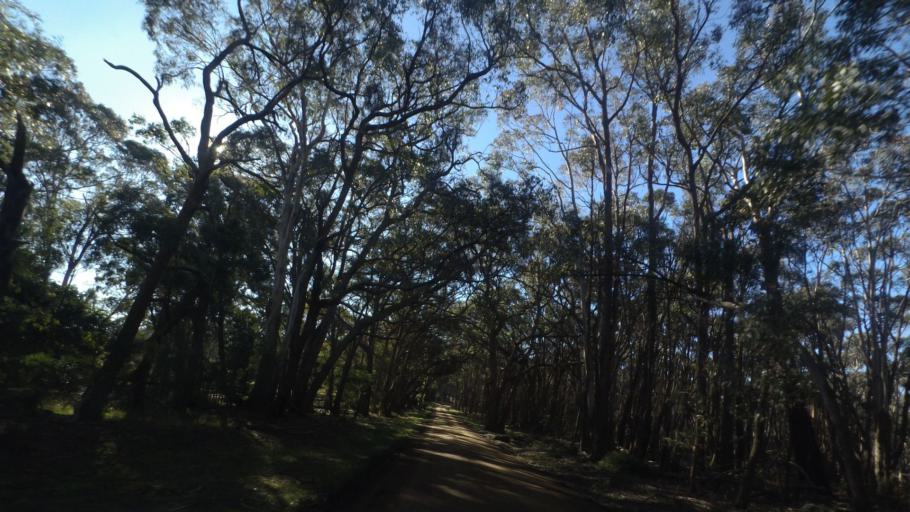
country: AU
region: Victoria
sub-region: Mount Alexander
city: Castlemaine
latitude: -37.2802
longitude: 144.3362
